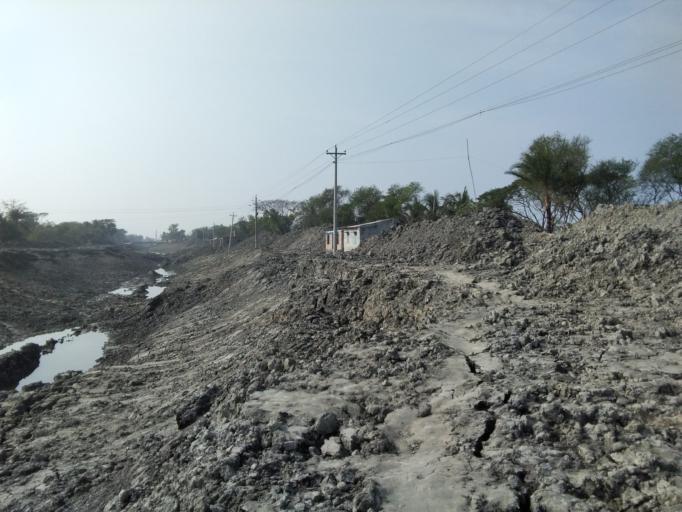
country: IN
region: West Bengal
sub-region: North 24 Parganas
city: Taki
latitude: 22.5918
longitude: 89.0338
